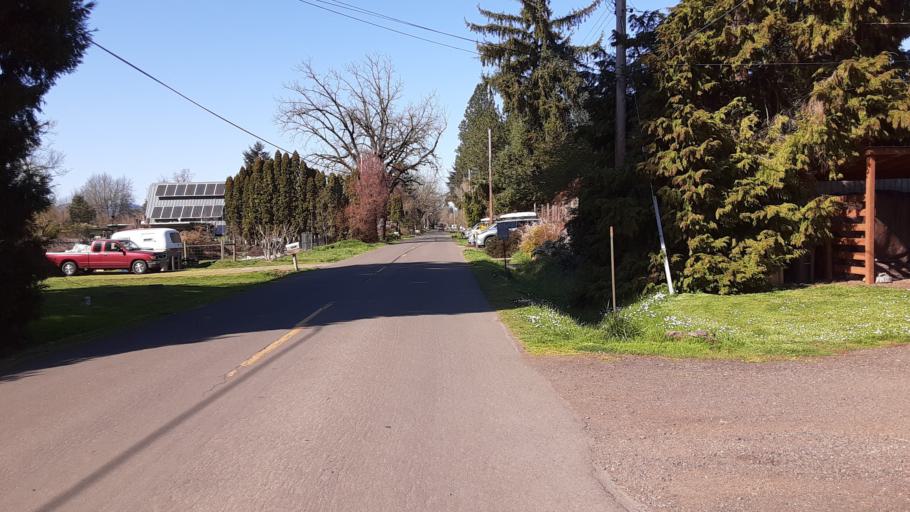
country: US
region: Oregon
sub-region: Benton County
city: Corvallis
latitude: 44.5399
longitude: -123.2556
